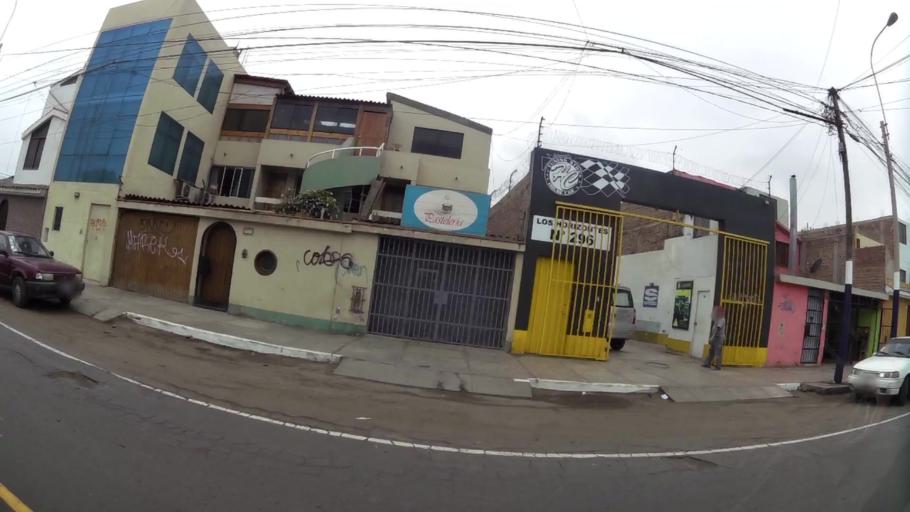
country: PE
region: Lima
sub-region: Lima
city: Surco
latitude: -12.2002
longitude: -77.0029
